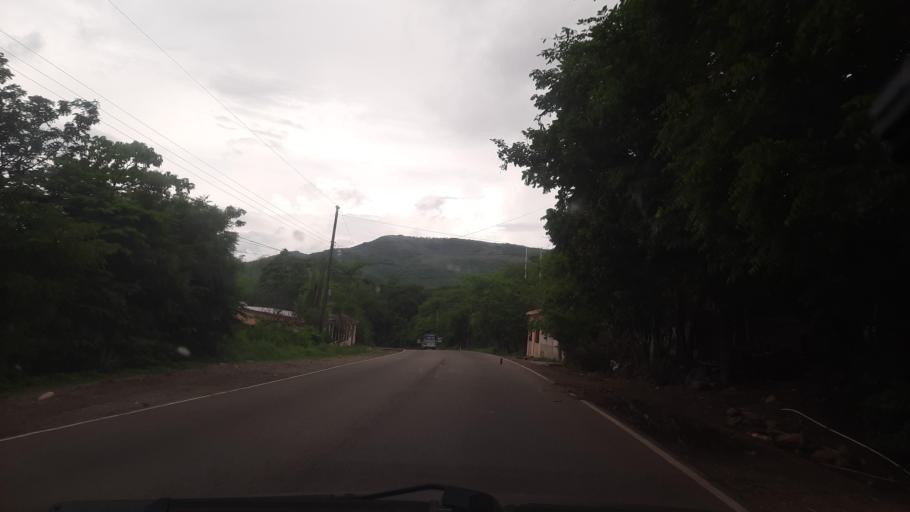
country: GT
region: Zacapa
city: San Jorge
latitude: 14.9118
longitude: -89.5296
